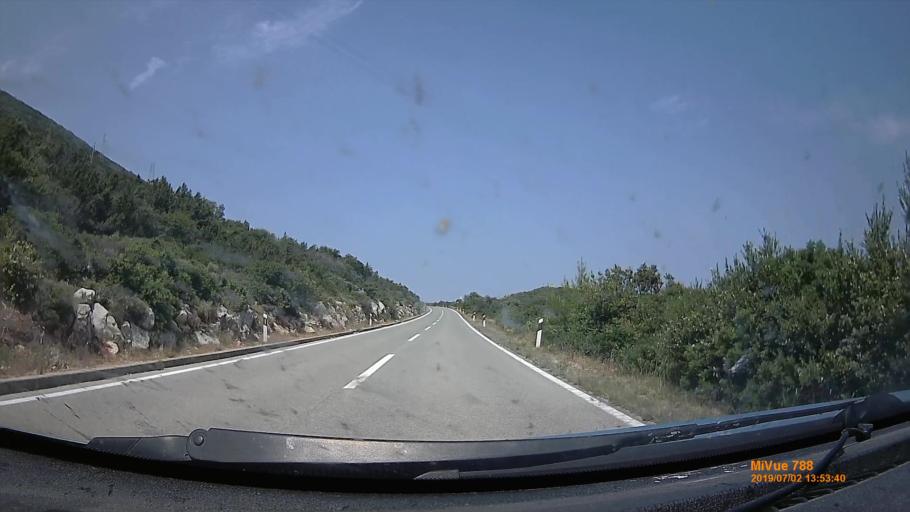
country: HR
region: Primorsko-Goranska
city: Mali Losinj
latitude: 44.6294
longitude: 14.3922
